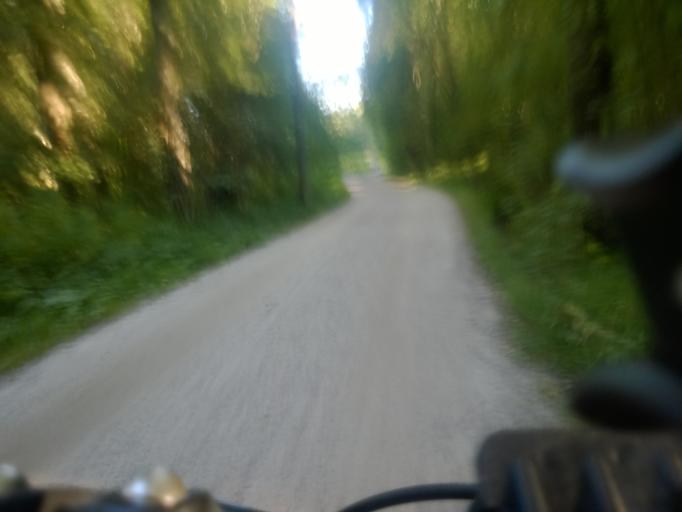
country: FI
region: Uusimaa
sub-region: Helsinki
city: Helsinki
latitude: 60.2067
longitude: 24.9098
